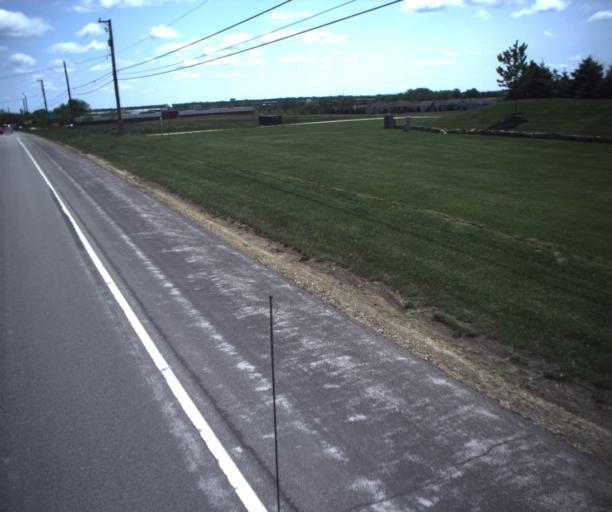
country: US
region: Illinois
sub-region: Kane County
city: Batavia
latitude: 41.8648
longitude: -88.3553
